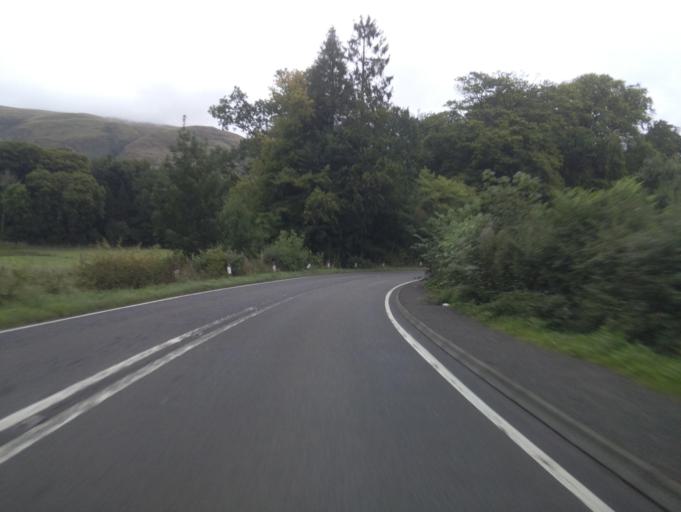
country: GB
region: Scotland
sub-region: Clackmannanshire
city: Tillicoultry
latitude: 56.1582
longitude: -3.7090
